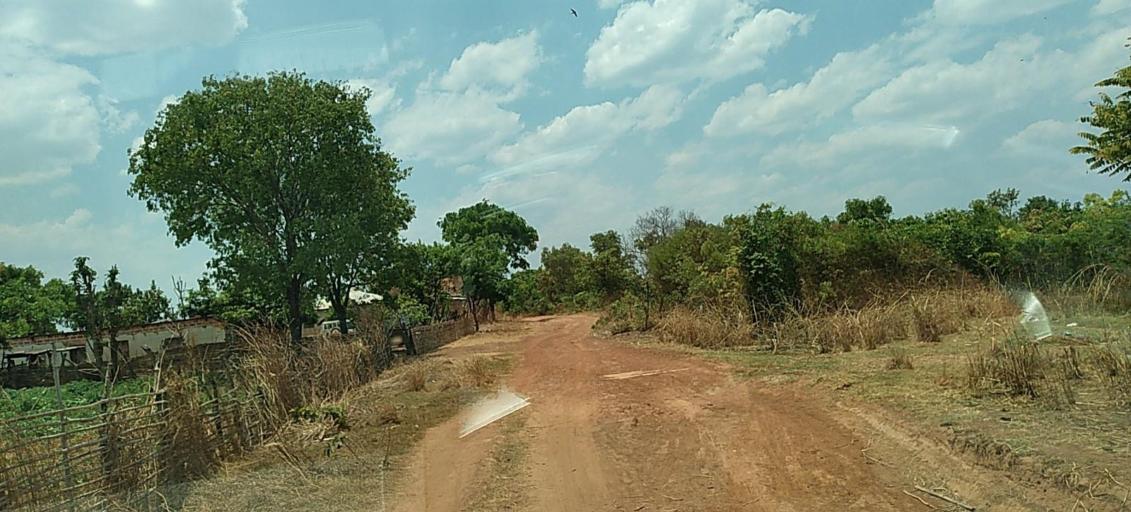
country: ZM
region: Copperbelt
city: Chingola
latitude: -12.5406
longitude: 27.6323
